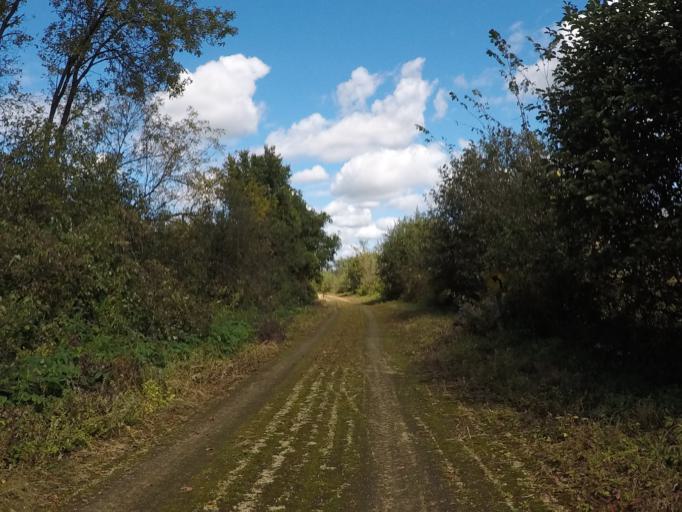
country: US
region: Wisconsin
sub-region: Richland County
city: Richland Center
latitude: 43.2604
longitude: -90.3017
